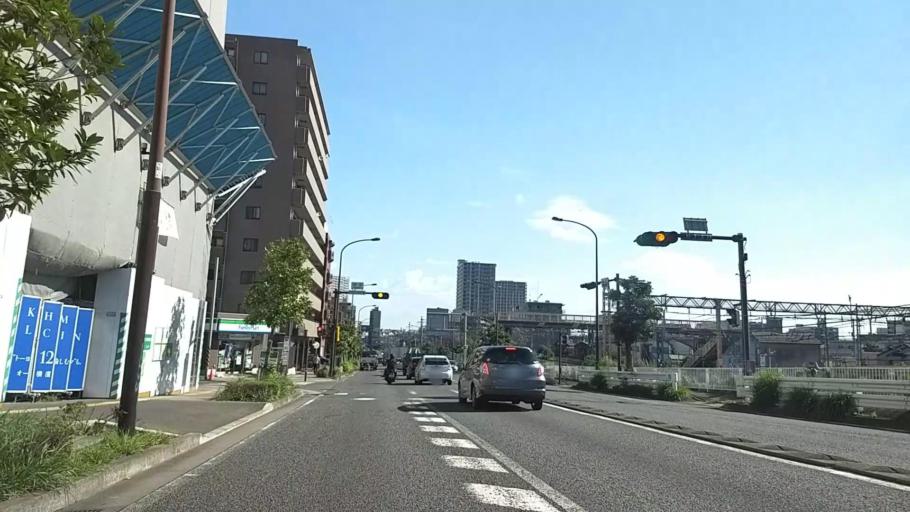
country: JP
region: Kanagawa
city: Yokohama
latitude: 35.4736
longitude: 139.6287
